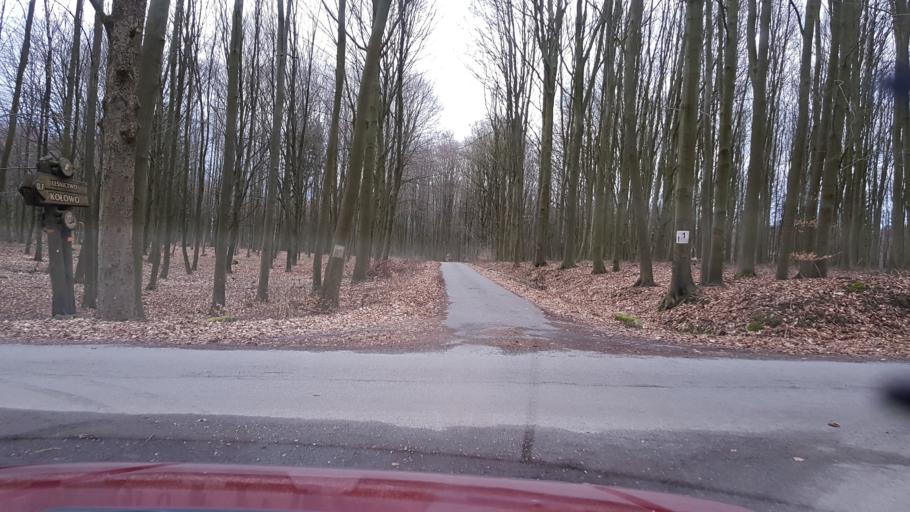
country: PL
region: West Pomeranian Voivodeship
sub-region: Powiat gryfinski
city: Stare Czarnowo
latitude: 53.3182
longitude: 14.7140
